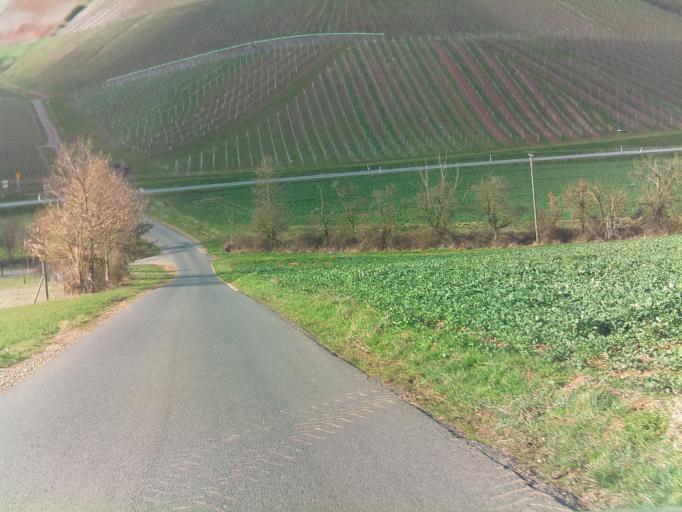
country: DE
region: Rheinland-Pfalz
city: Kirschroth
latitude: 49.7608
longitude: 7.5817
